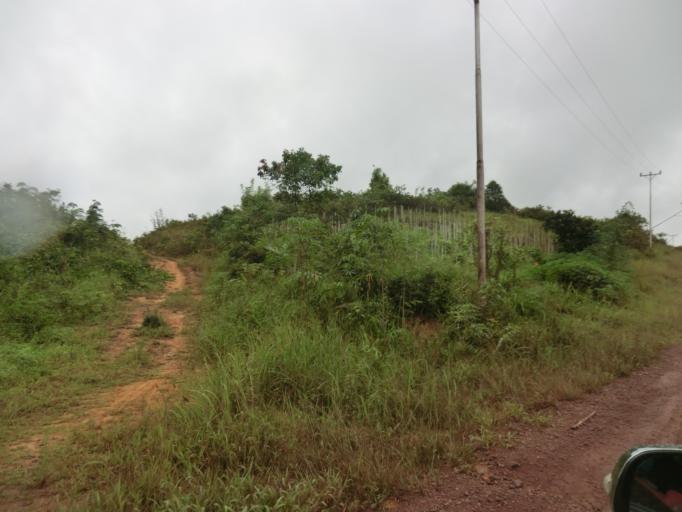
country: MY
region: Sarawak
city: Simanggang
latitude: 1.0775
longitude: 111.9773
